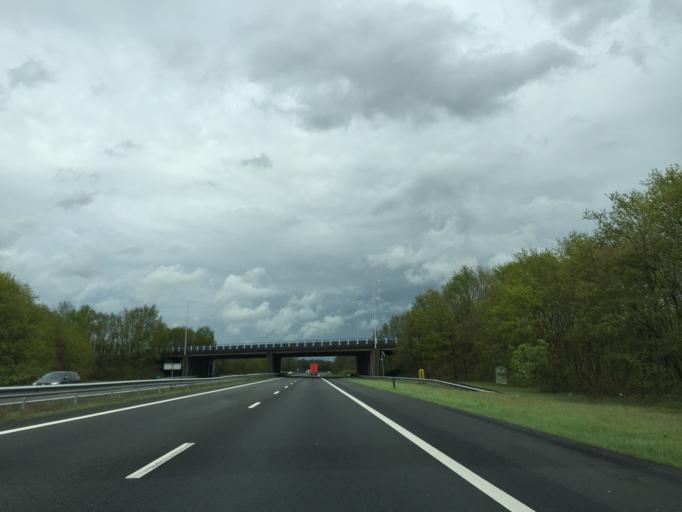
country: NL
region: Gelderland
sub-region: Gemeente Harderwijk
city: Harderwijk
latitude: 52.3364
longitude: 5.6434
